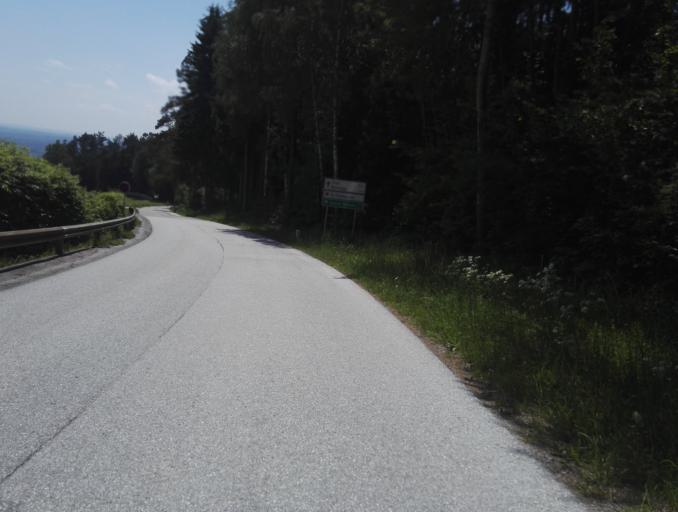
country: AT
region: Styria
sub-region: Politischer Bezirk Graz-Umgebung
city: Sankt Radegund bei Graz
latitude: 47.1878
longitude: 15.4811
